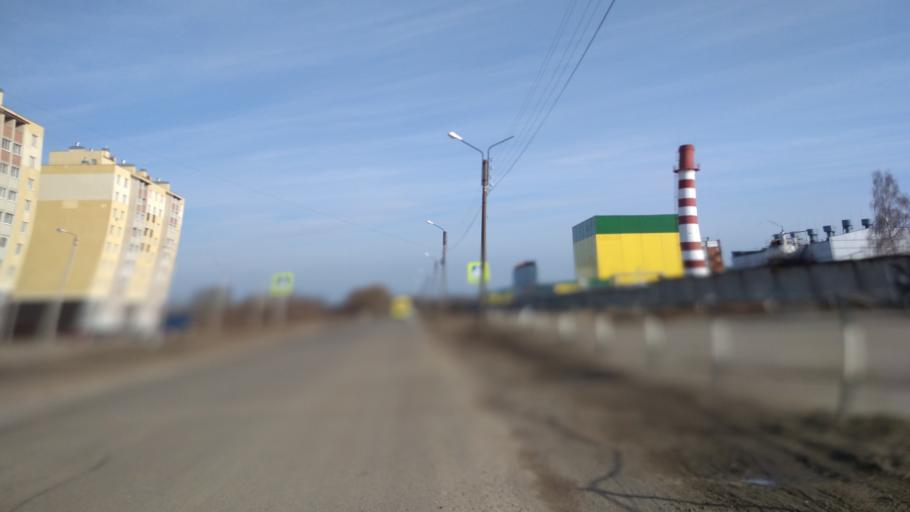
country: RU
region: Chuvashia
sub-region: Cheboksarskiy Rayon
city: Cheboksary
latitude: 56.1370
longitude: 47.3107
